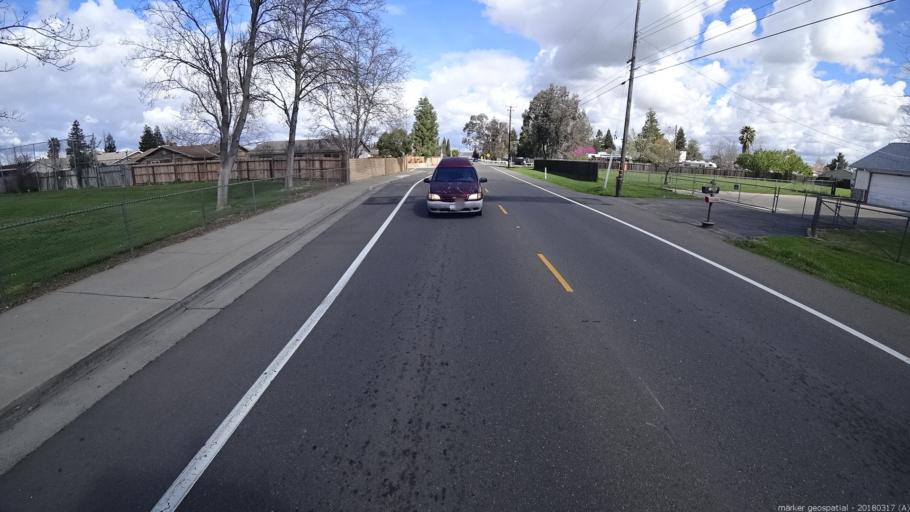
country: US
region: California
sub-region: Sacramento County
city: Florin
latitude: 38.4705
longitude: -121.3903
